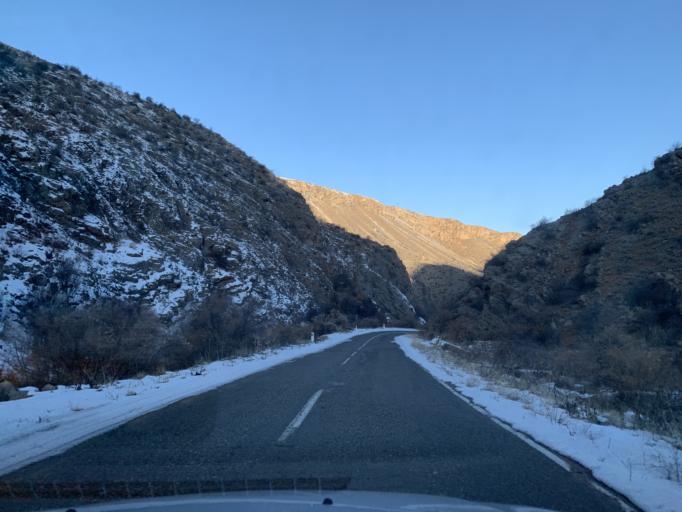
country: AM
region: Vayots' Dzori Marz
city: Areni
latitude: 39.6923
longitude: 45.2158
